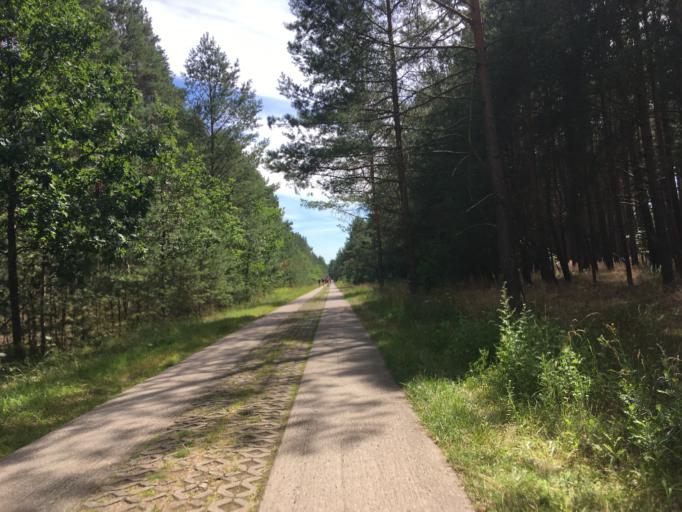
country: DE
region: Brandenburg
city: Rheinsberg
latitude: 53.0491
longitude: 12.9066
